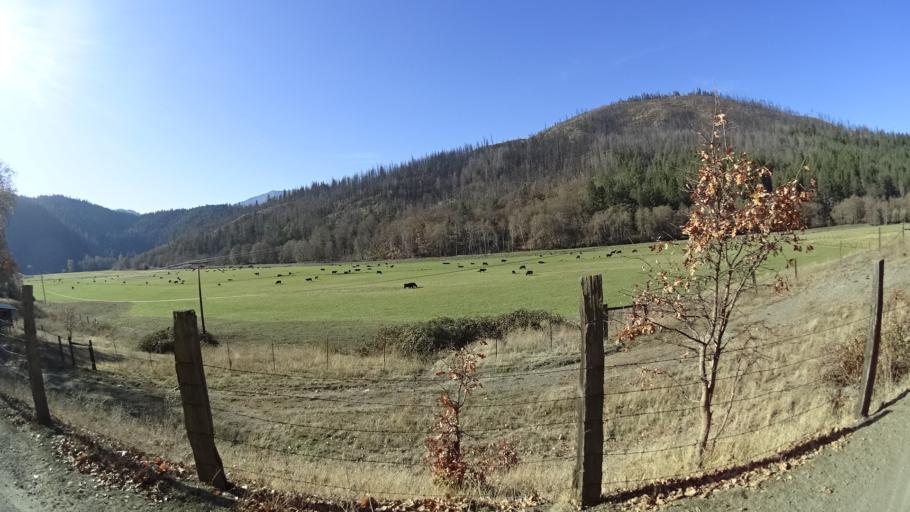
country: US
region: California
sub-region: Siskiyou County
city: Happy Camp
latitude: 41.8326
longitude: -123.0046
